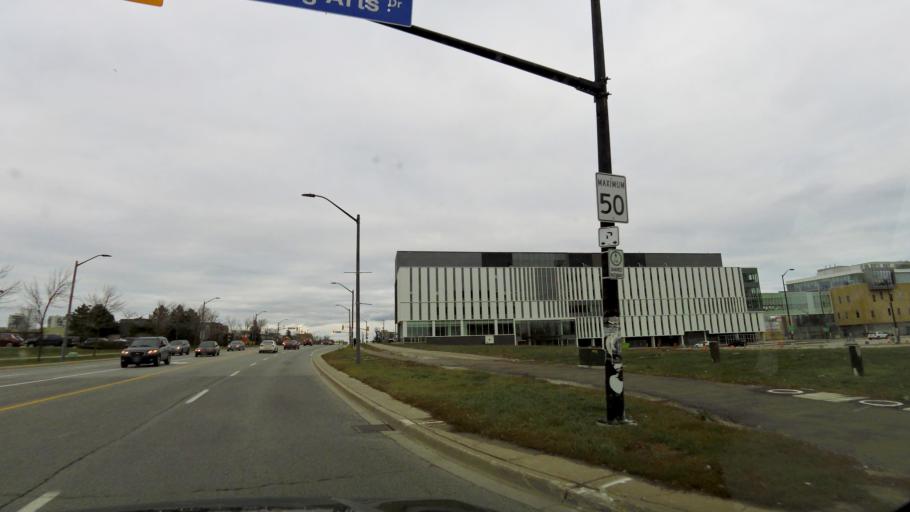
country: CA
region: Ontario
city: Mississauga
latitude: 43.5913
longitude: -79.6501
